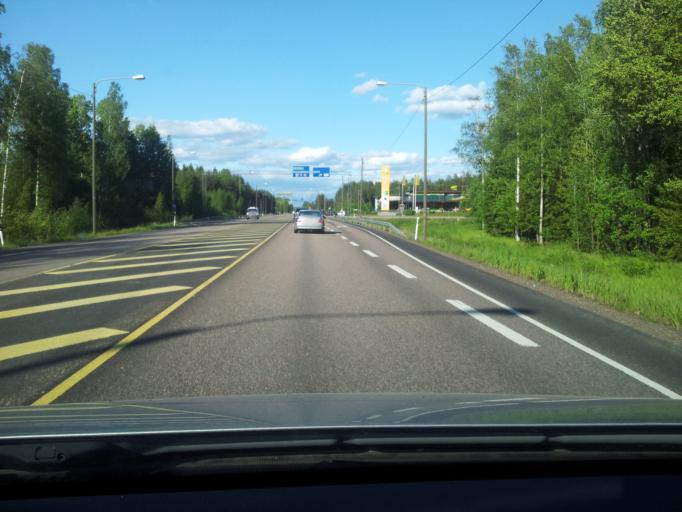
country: FI
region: Kymenlaakso
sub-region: Kouvola
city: Kouvola
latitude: 60.8587
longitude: 26.5629
